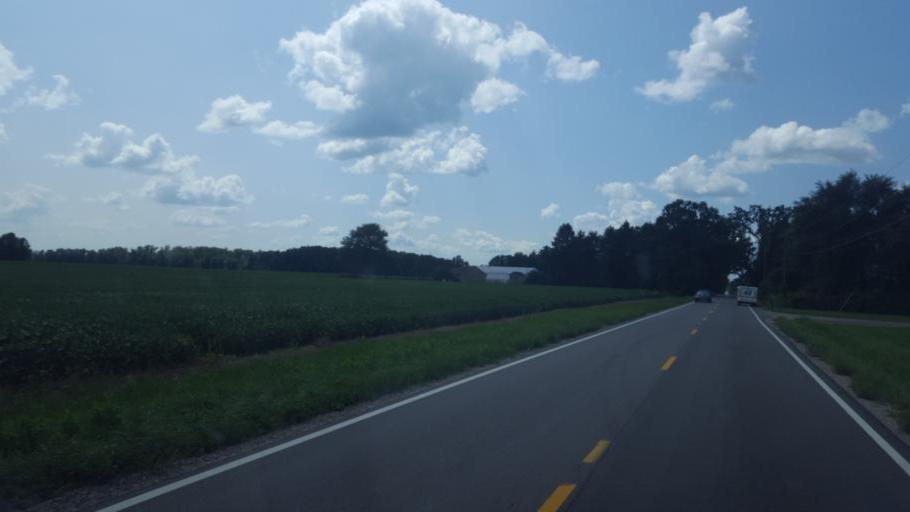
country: US
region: Ohio
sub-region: Delaware County
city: Ashley
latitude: 40.3358
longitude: -82.9017
